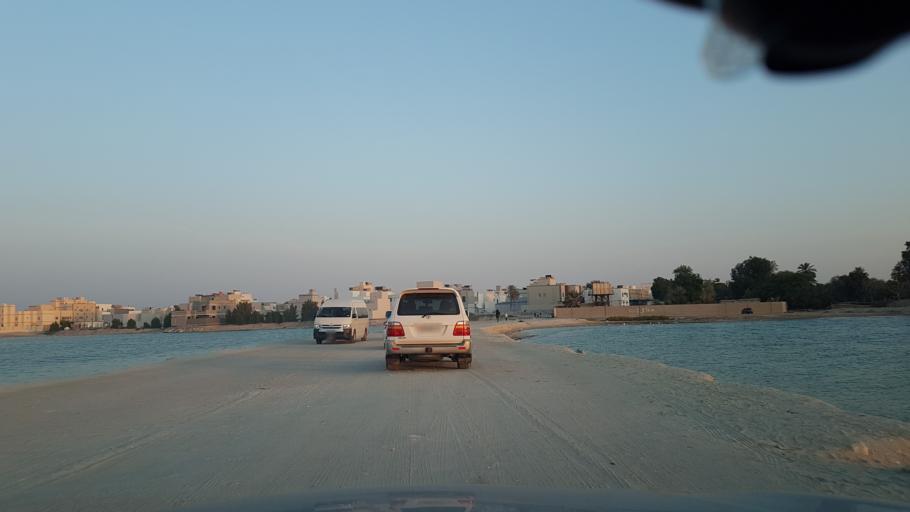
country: BH
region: Manama
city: Jidd Hafs
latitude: 26.2375
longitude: 50.5049
